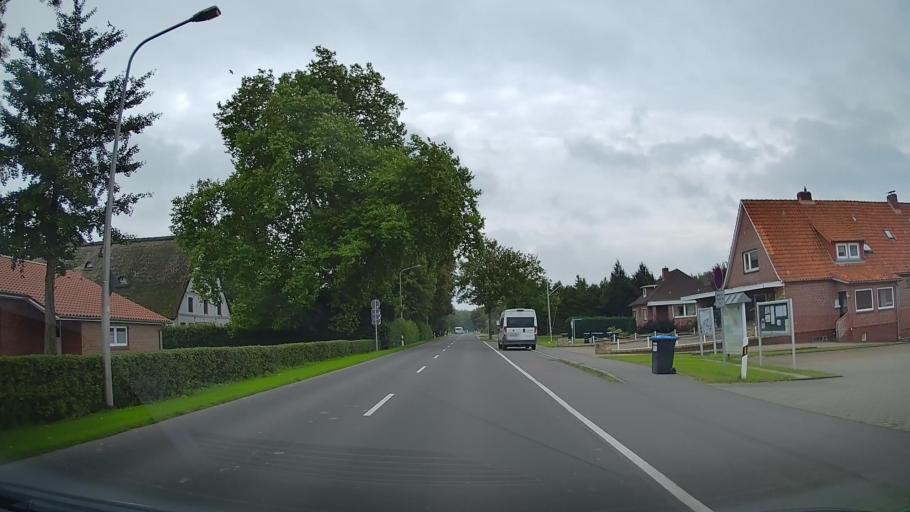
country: DE
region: Lower Saxony
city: Drochtersen
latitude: 53.7336
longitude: 9.3475
